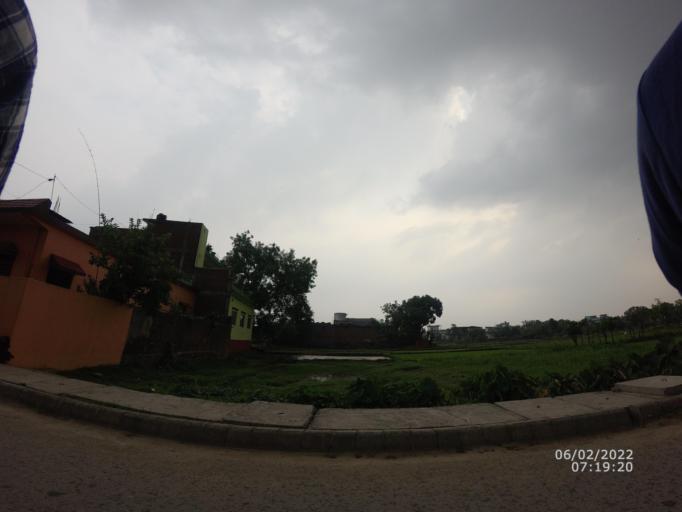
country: NP
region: Western Region
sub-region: Lumbini Zone
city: Bhairahawa
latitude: 27.4852
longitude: 83.4392
